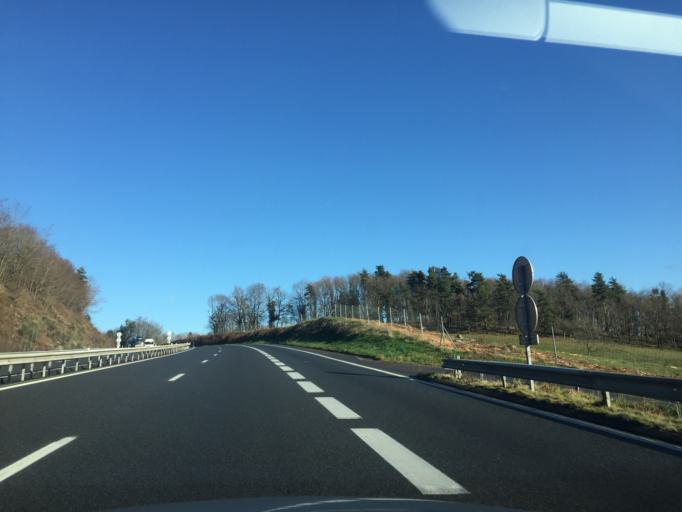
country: FR
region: Auvergne
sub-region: Departement du Puy-de-Dome
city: Thiers
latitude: 45.8736
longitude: 3.5638
